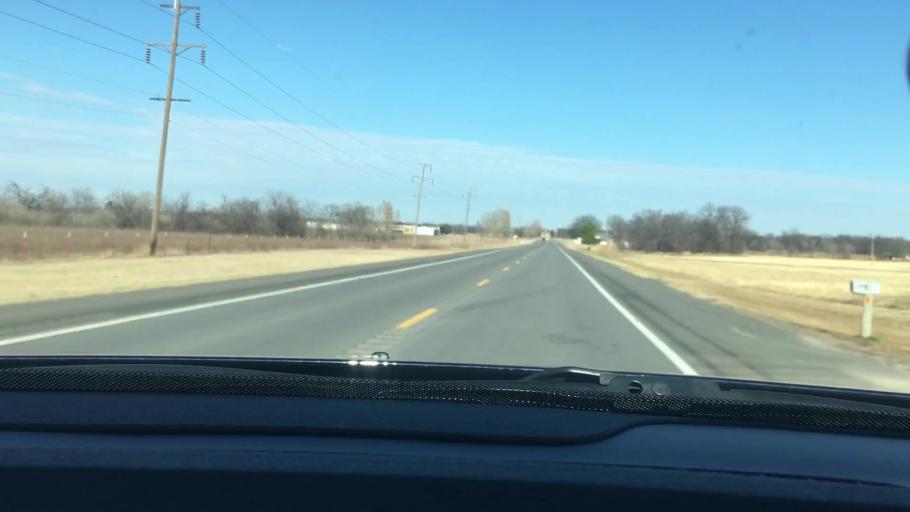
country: US
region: Oklahoma
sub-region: Garvin County
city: Wynnewood
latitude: 34.5880
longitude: -97.1425
